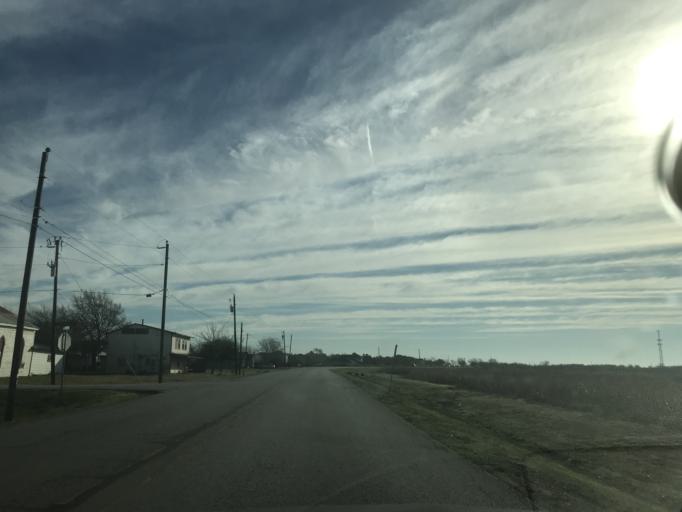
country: US
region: Texas
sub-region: Travis County
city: Manor
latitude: 30.3372
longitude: -97.5558
